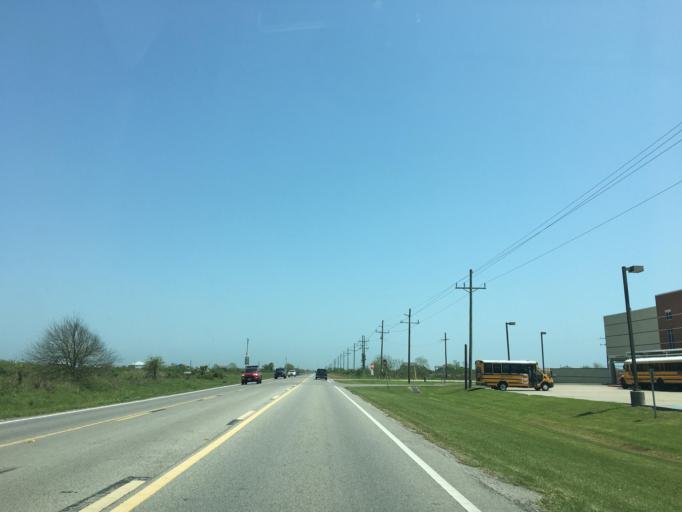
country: US
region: Texas
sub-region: Galveston County
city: Bolivar Peninsula
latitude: 29.4279
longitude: -94.6907
